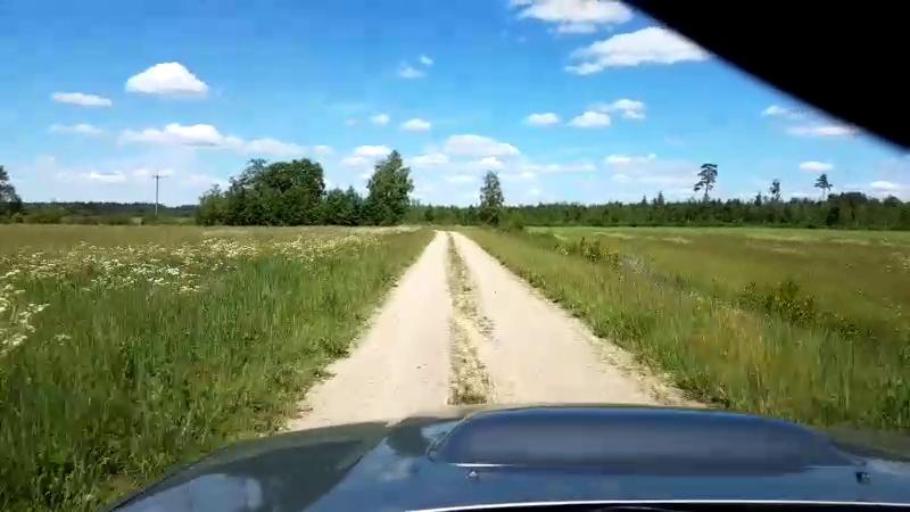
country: EE
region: Paernumaa
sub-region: Halinga vald
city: Parnu-Jaagupi
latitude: 58.5360
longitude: 24.5301
